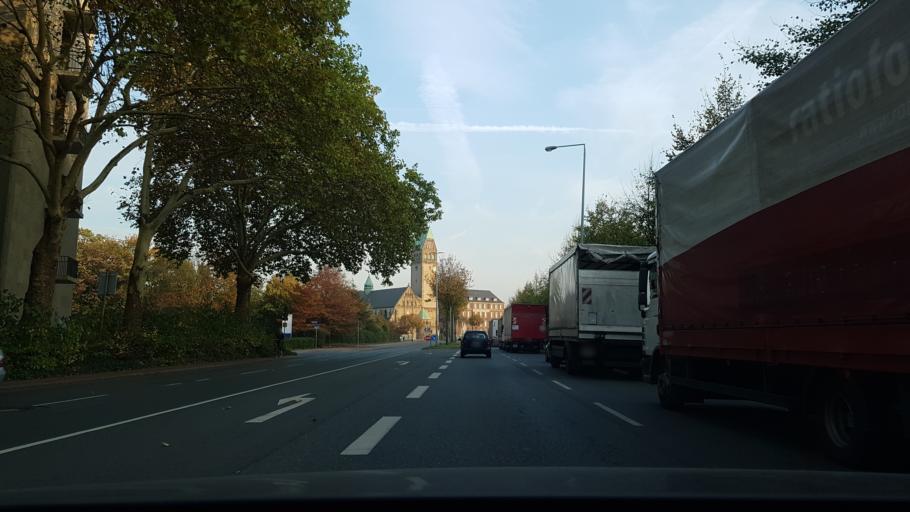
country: DE
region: North Rhine-Westphalia
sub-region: Regierungsbezirk Dusseldorf
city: Hochfeld
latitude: 51.4158
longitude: 6.7496
